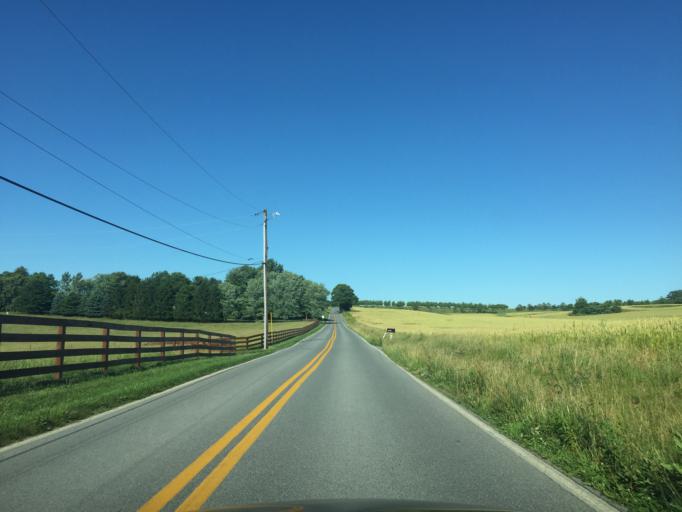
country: US
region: Maryland
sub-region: Carroll County
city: Hampstead
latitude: 39.5531
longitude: -76.8529
